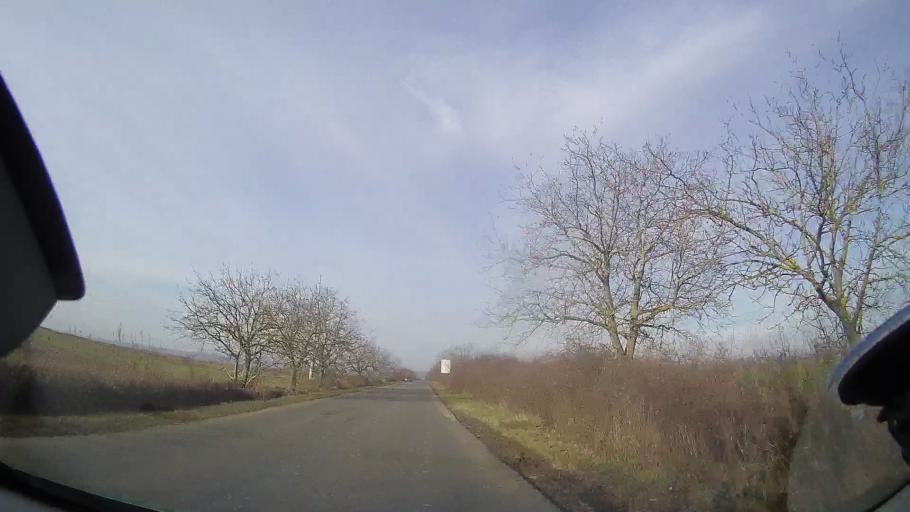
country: RO
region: Bihor
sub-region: Comuna Spinus
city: Spinus
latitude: 47.2202
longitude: 22.1722
